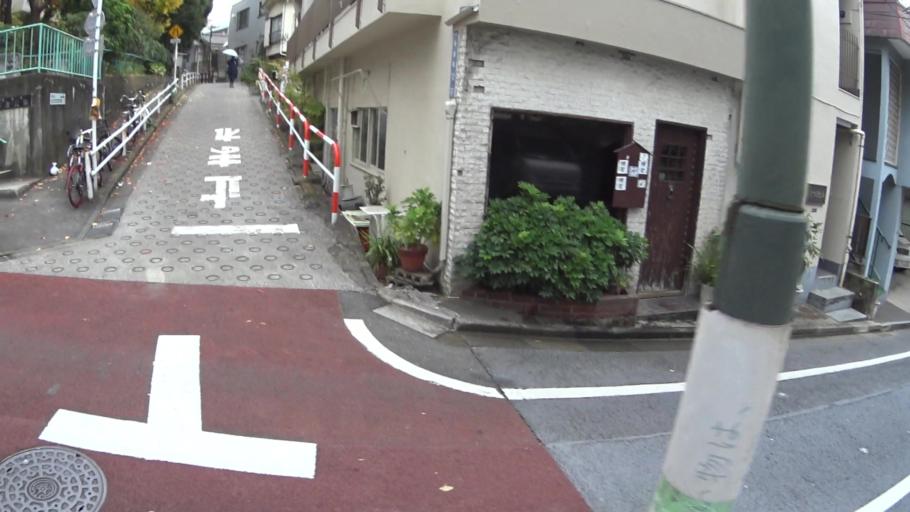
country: JP
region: Tokyo
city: Tokyo
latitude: 35.6939
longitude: 139.7202
